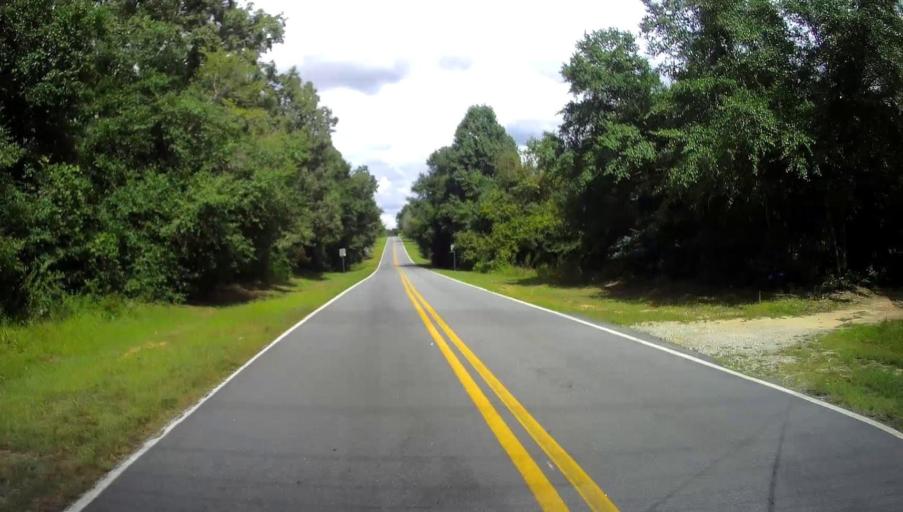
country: US
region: Georgia
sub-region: Chattahoochee County
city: Cusseta
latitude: 32.3067
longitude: -84.7669
